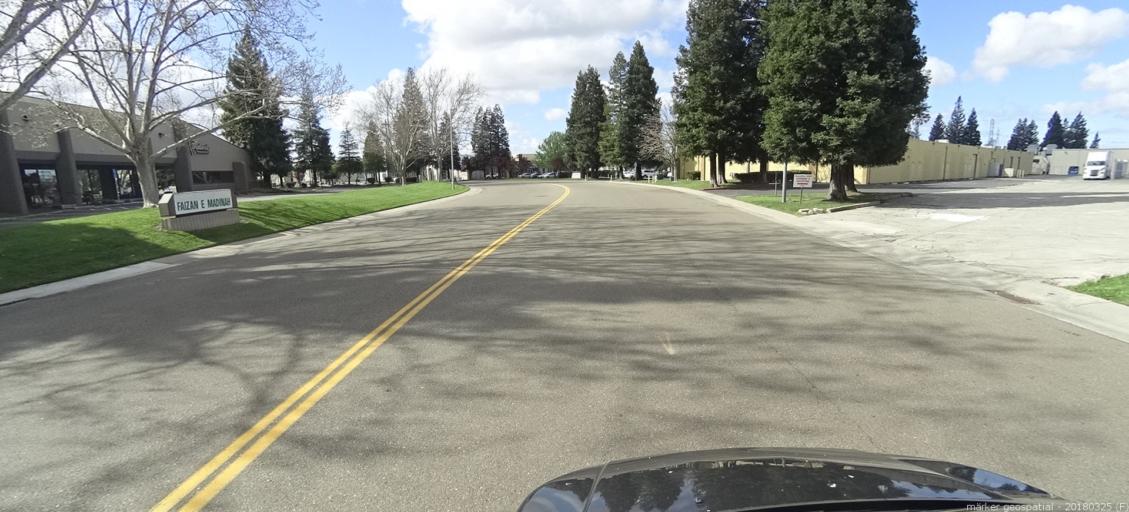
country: US
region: California
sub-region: Sacramento County
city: Rio Linda
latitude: 38.6446
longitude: -121.4784
